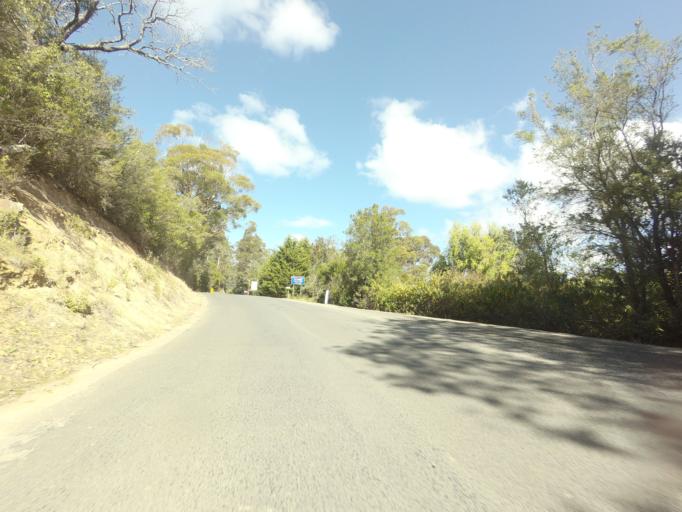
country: AU
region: Tasmania
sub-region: Break O'Day
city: St Helens
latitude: -41.6324
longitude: 148.2363
